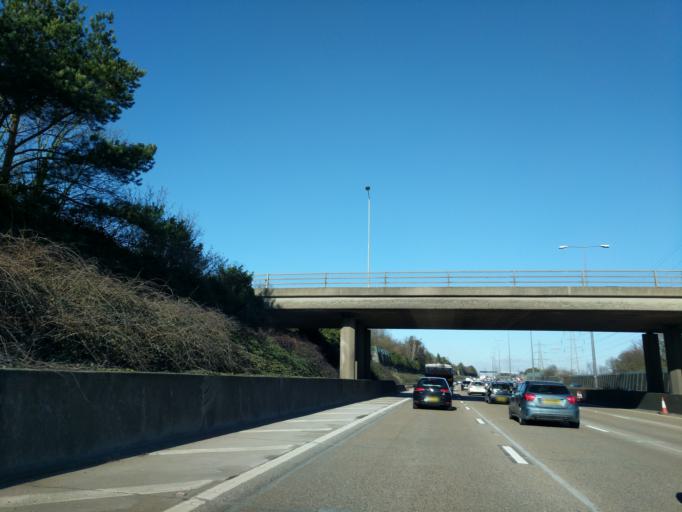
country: GB
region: England
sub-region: Surrey
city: Byfleet
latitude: 51.3395
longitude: -0.4853
